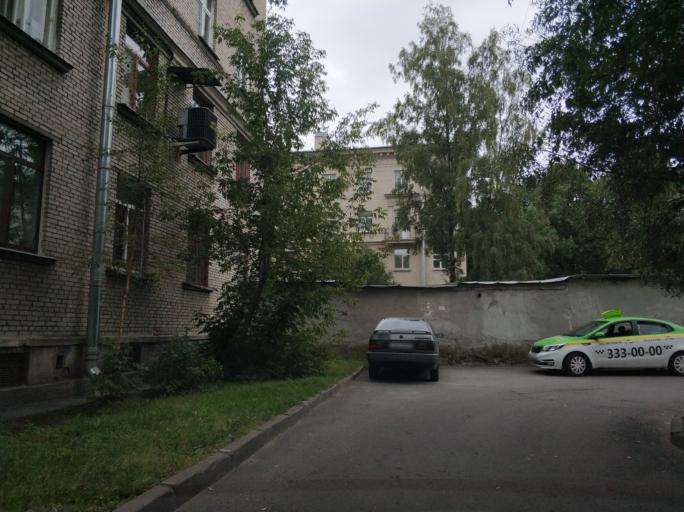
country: RU
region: St.-Petersburg
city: Novaya Derevnya
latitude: 59.9869
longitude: 30.2911
